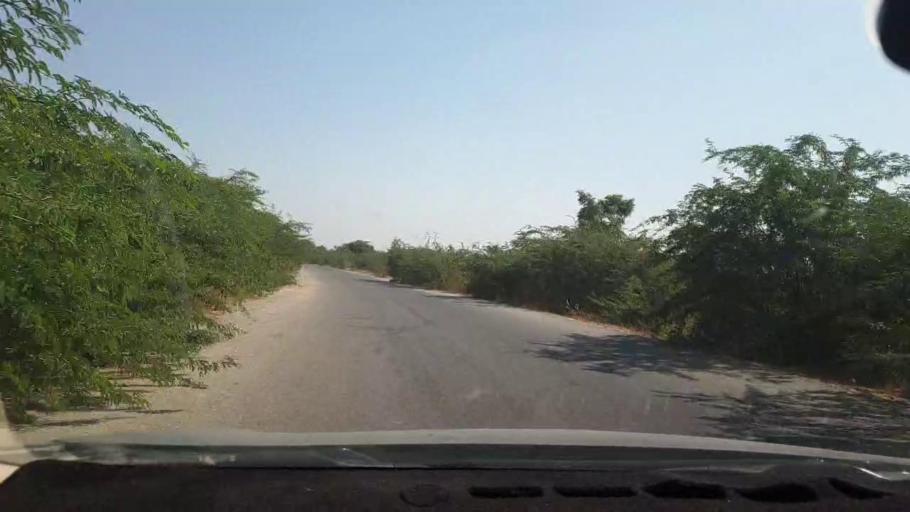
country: PK
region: Sindh
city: Malir Cantonment
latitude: 25.1422
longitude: 67.1951
